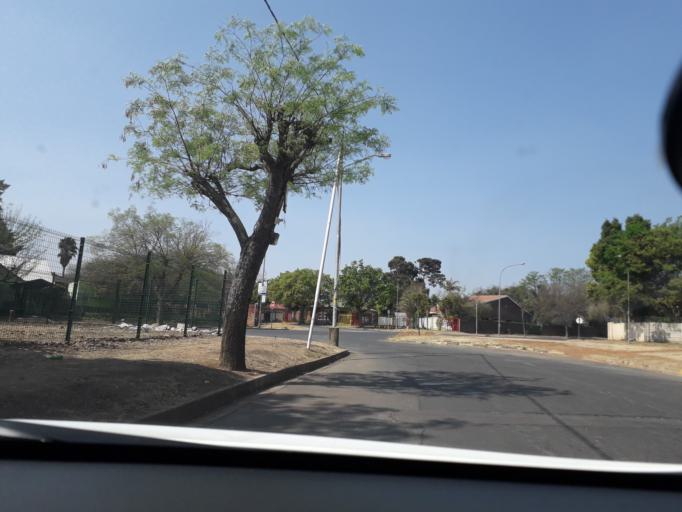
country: ZA
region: Gauteng
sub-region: City of Johannesburg Metropolitan Municipality
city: Modderfontein
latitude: -26.0928
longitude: 28.2296
